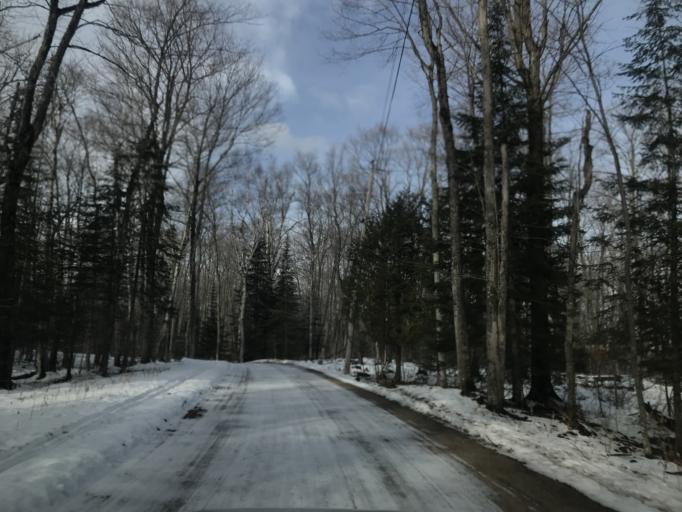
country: US
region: Wisconsin
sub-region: Door County
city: Sturgeon Bay
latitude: 45.1548
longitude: -87.0431
